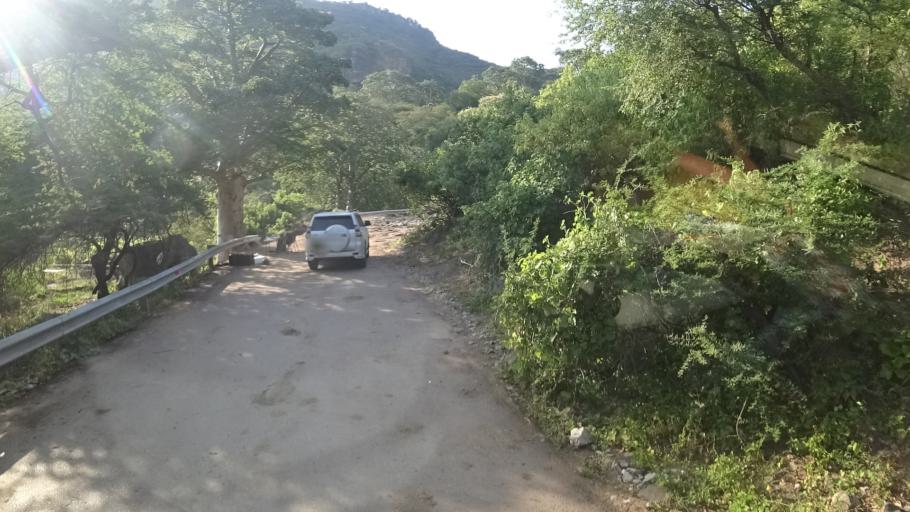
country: OM
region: Zufar
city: Salalah
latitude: 17.0532
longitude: 54.6103
